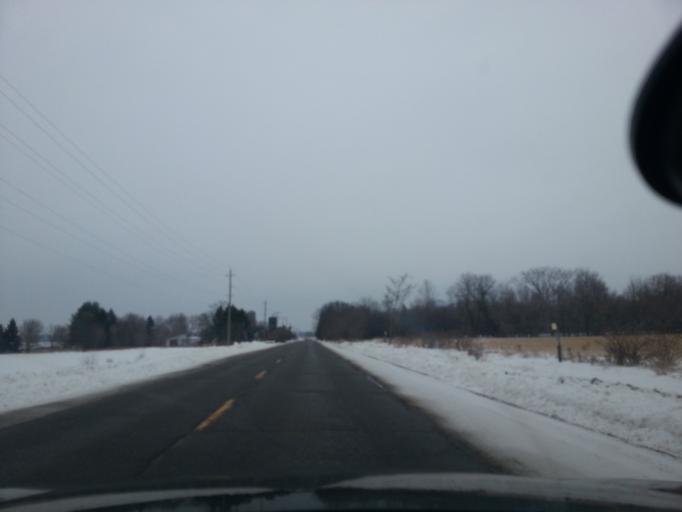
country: CA
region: Ontario
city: Arnprior
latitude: 45.3787
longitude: -76.2099
